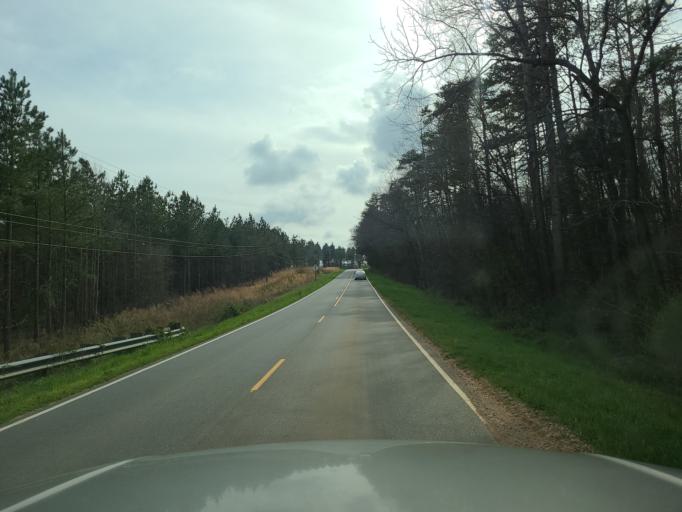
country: US
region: North Carolina
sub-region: Cleveland County
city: Boiling Springs
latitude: 35.2496
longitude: -81.7145
